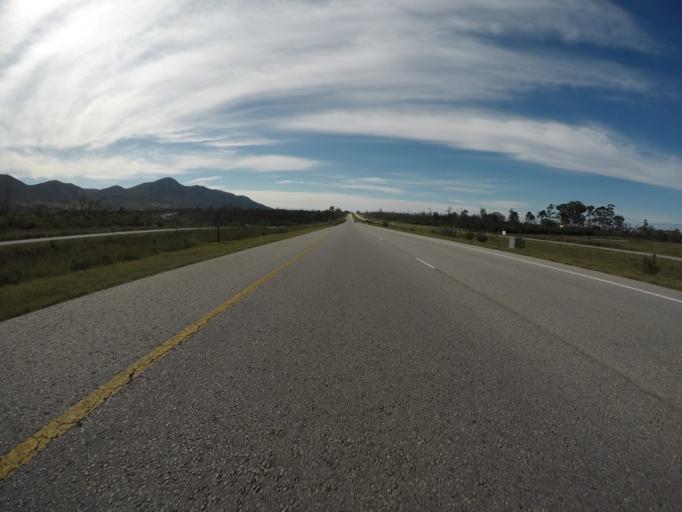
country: ZA
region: Eastern Cape
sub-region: Nelson Mandela Bay Metropolitan Municipality
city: Uitenhage
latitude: -33.9094
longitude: 25.2266
